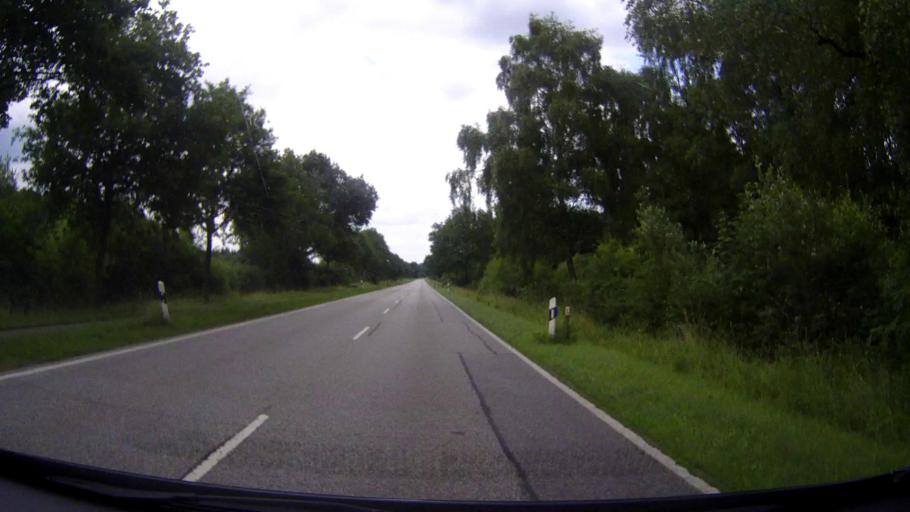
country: DE
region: Schleswig-Holstein
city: Hohenwestedt
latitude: 54.0849
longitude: 9.6771
